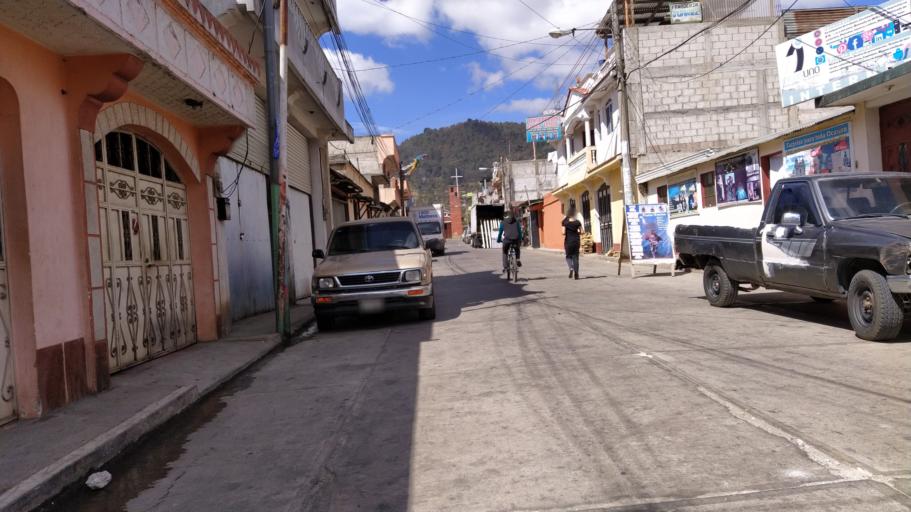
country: GT
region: Quetzaltenango
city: Ostuncalco
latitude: 14.8694
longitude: -91.6246
